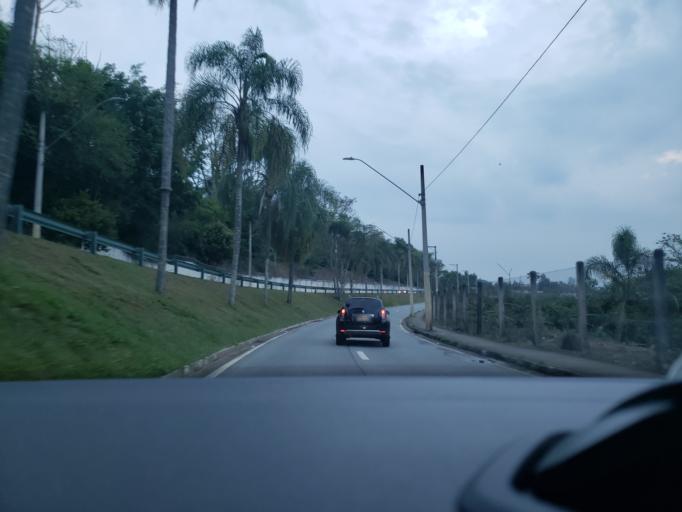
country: BR
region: Sao Paulo
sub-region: Sao Jose Dos Campos
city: Sao Jose dos Campos
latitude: -23.1950
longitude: -45.9384
